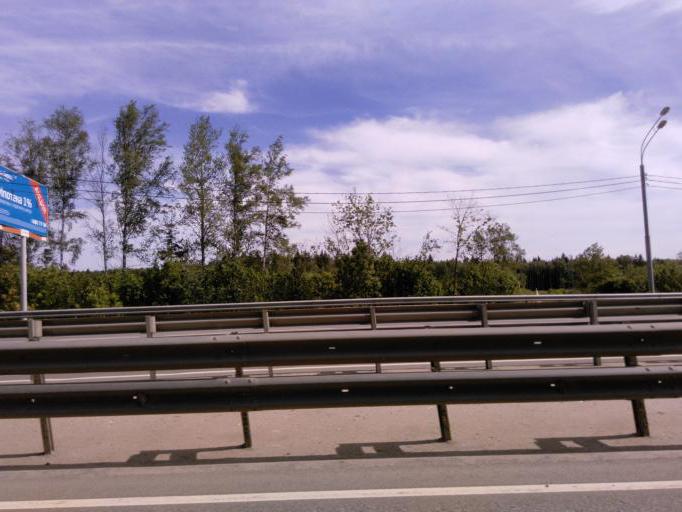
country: RU
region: Moskovskaya
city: Rzhavki
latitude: 55.9916
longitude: 37.2653
